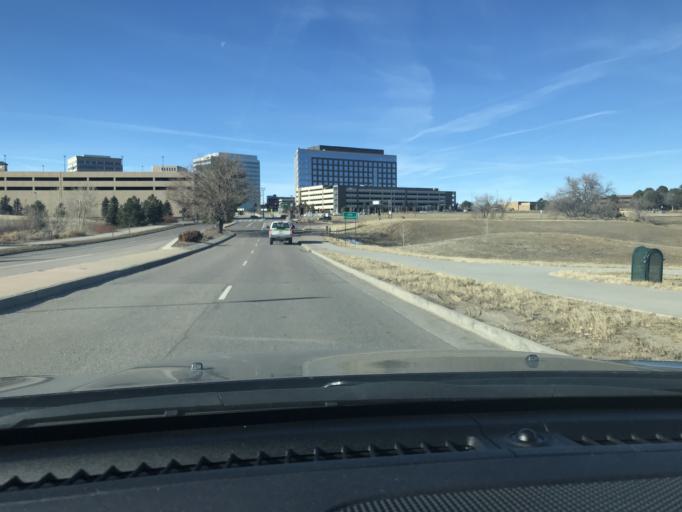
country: US
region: Colorado
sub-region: Arapahoe County
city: Centennial
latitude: 39.6024
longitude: -104.8833
